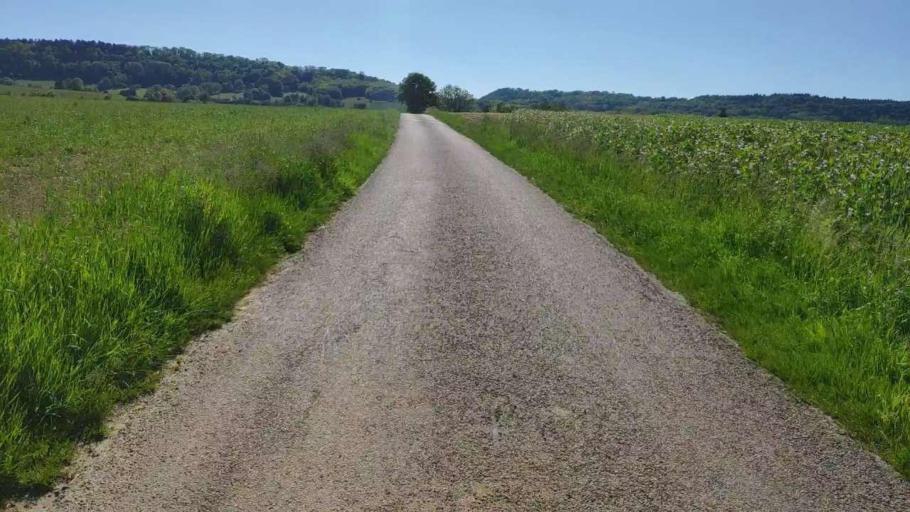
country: FR
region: Franche-Comte
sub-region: Departement du Jura
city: Lons-le-Saunier
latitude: 46.7271
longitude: 5.5658
